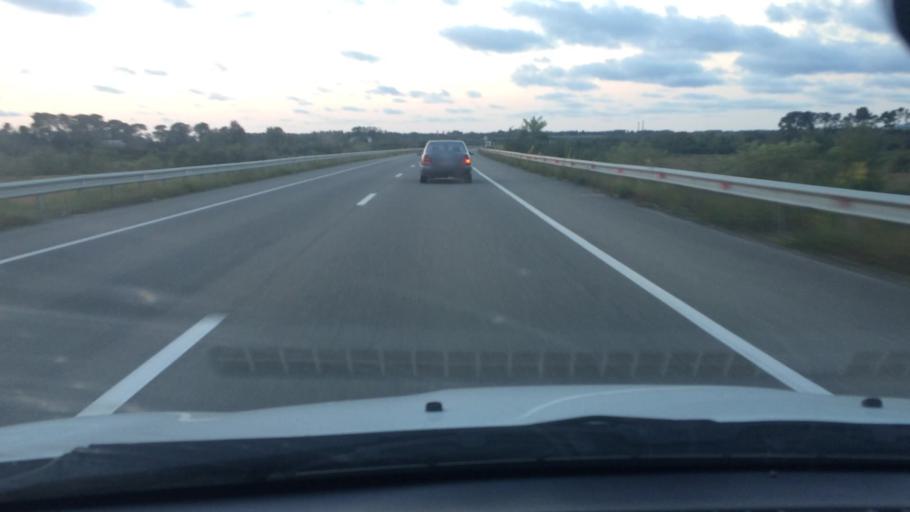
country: GE
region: Guria
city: Urek'i
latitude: 41.9118
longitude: 41.7810
